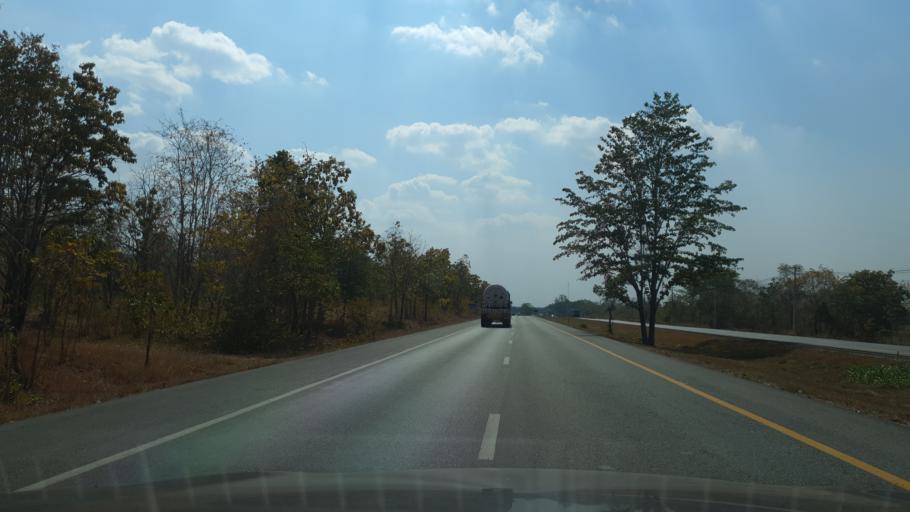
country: TH
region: Lampang
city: Mae Phrik
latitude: 17.3165
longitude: 99.1506
